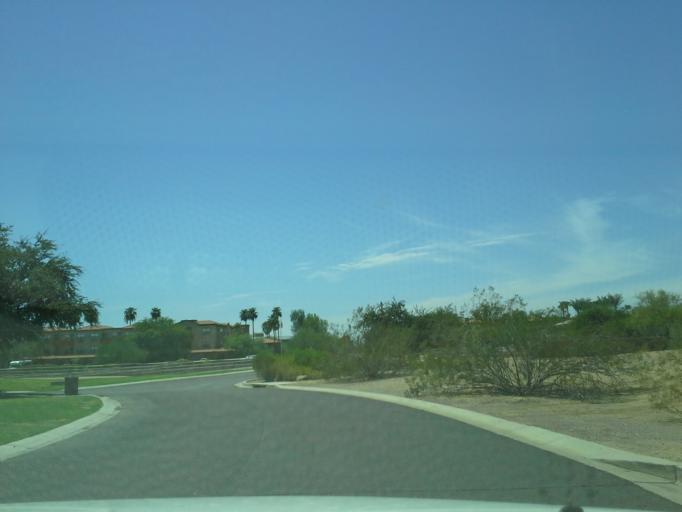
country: US
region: Arizona
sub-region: Maricopa County
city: Scottsdale
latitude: 33.5853
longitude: -111.8815
